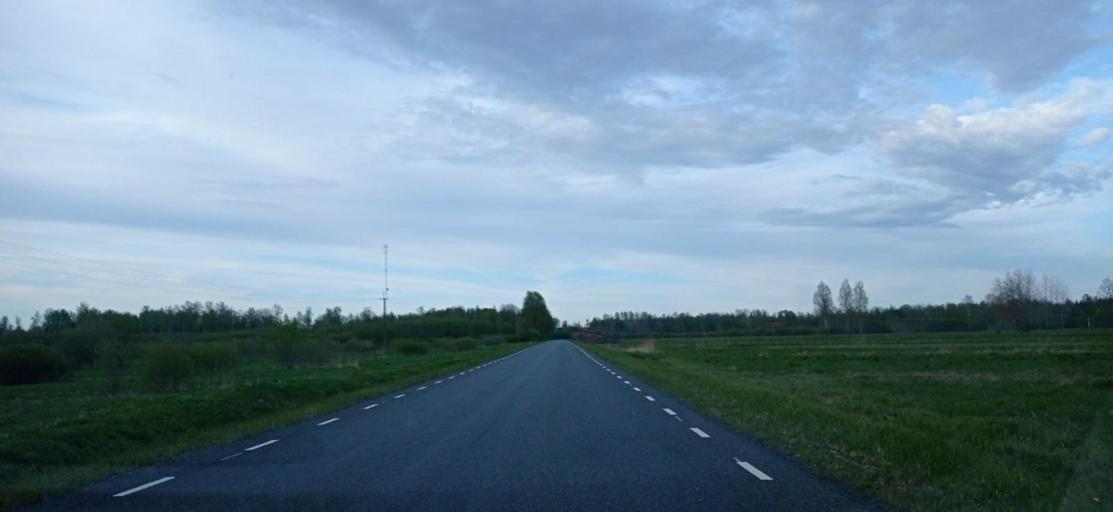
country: EE
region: Paernumaa
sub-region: Tootsi vald
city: Tootsi
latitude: 58.5617
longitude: 24.7984
